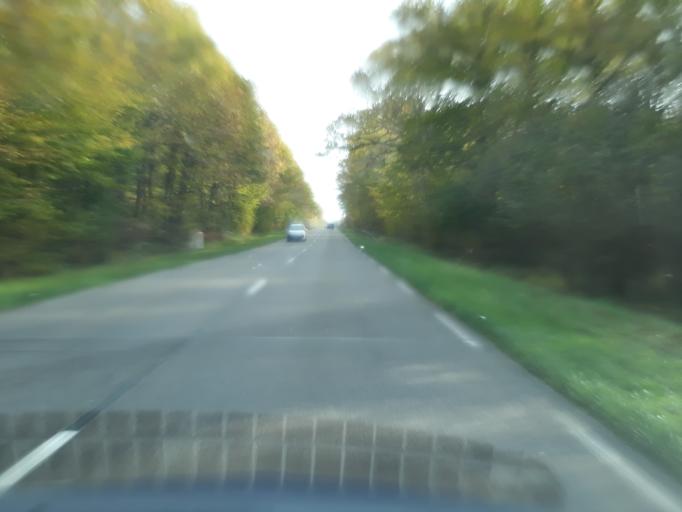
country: FR
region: Ile-de-France
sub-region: Departement de Seine-et-Marne
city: Champagne-sur-Seine
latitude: 48.4197
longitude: 2.8173
